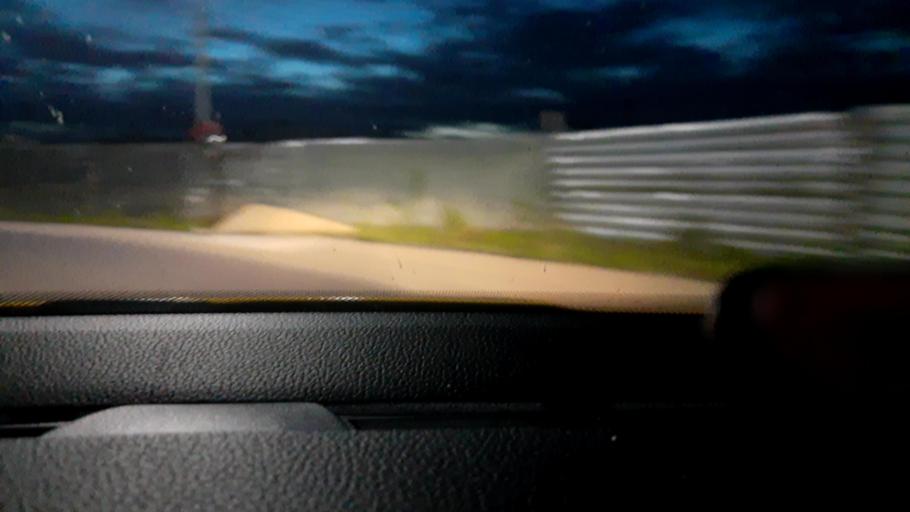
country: RU
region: Moskovskaya
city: Pirogovskiy
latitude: 55.9578
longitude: 37.6742
